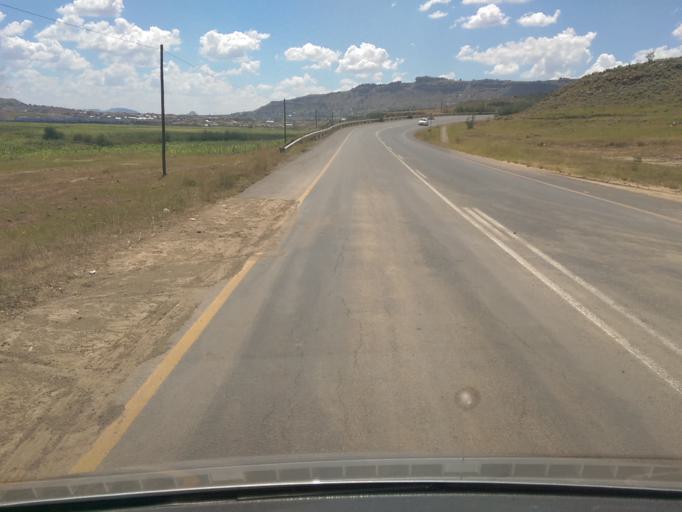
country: LS
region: Maseru
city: Maseru
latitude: -29.3872
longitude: 27.5043
